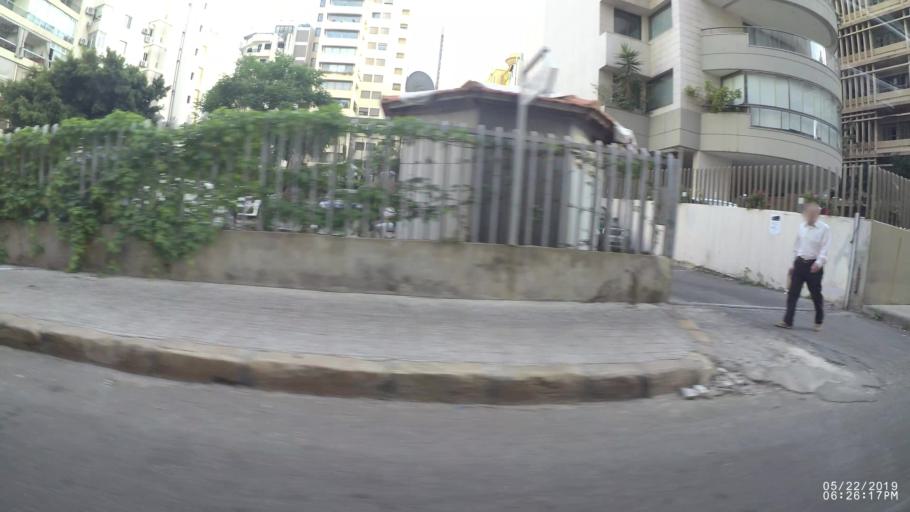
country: LB
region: Beyrouth
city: Beirut
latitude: 33.8976
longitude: 35.4932
